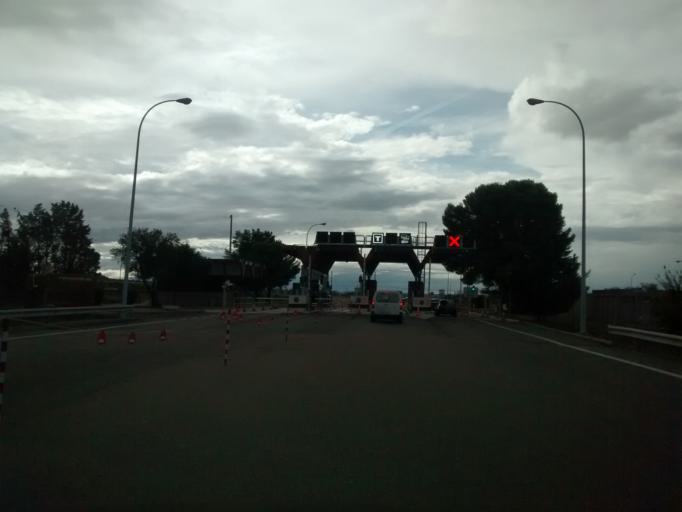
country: ES
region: Navarre
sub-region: Provincia de Navarra
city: Murchante
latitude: 42.0328
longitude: -1.6325
